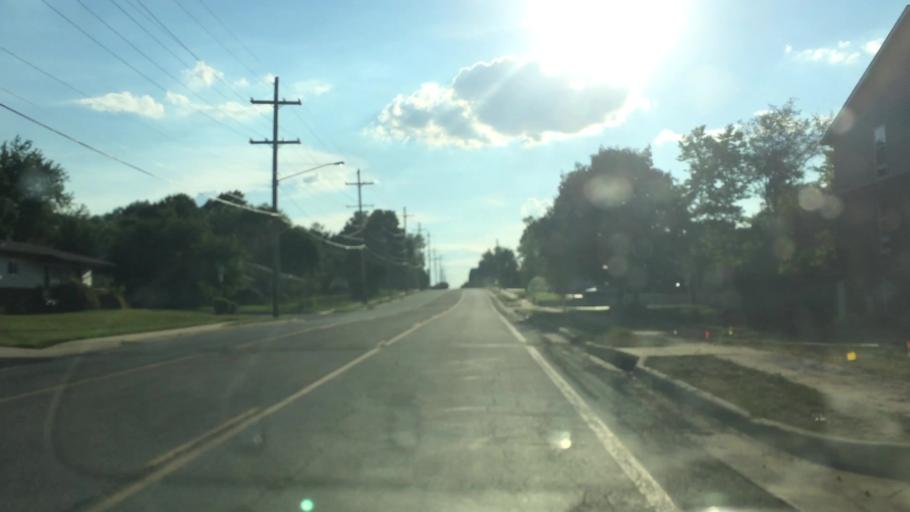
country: US
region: Missouri
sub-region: Greene County
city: Springfield
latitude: 37.2035
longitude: -93.2569
